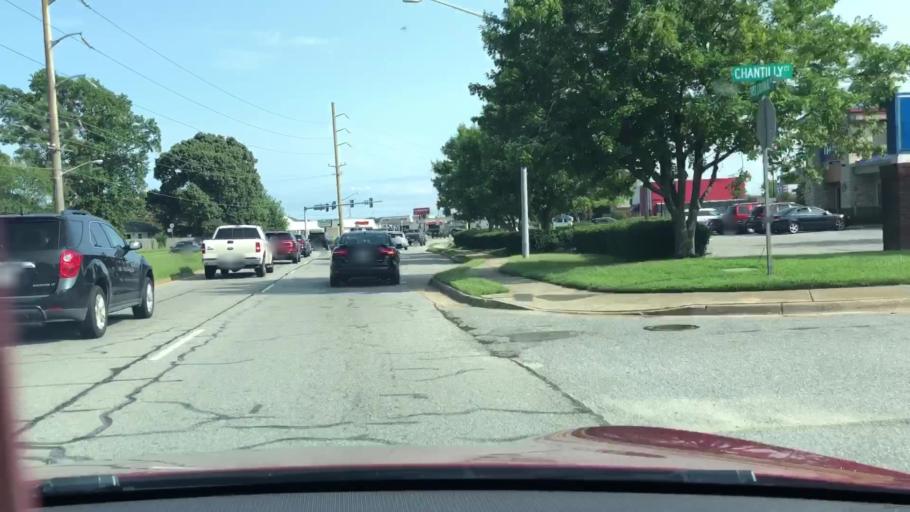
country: US
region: Virginia
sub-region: City of Virginia Beach
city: Virginia Beach
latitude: 36.8542
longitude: -76.0238
